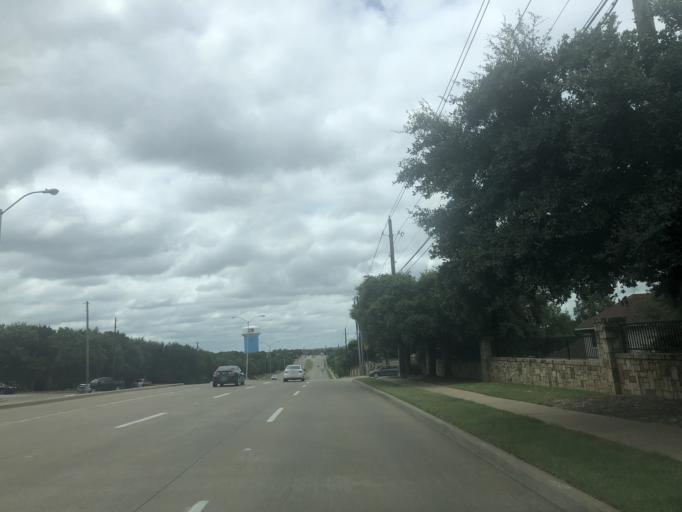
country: US
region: Texas
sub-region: Dallas County
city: Duncanville
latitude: 32.6569
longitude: -96.9432
